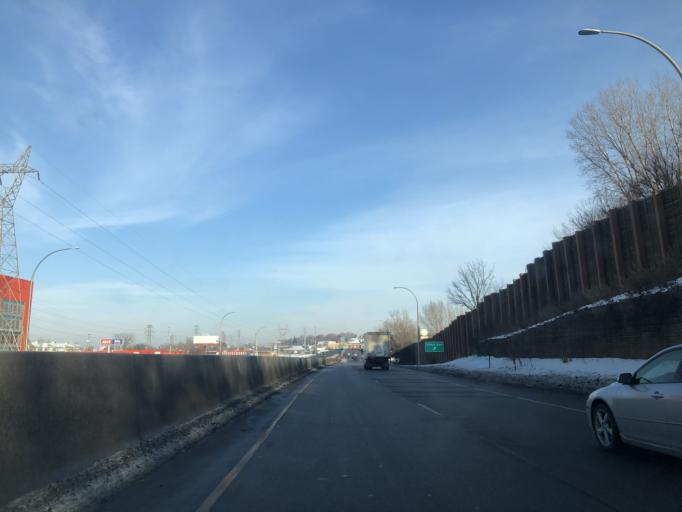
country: US
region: Minnesota
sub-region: Ramsey County
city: Lauderdale
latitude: 44.9821
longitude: -93.2034
